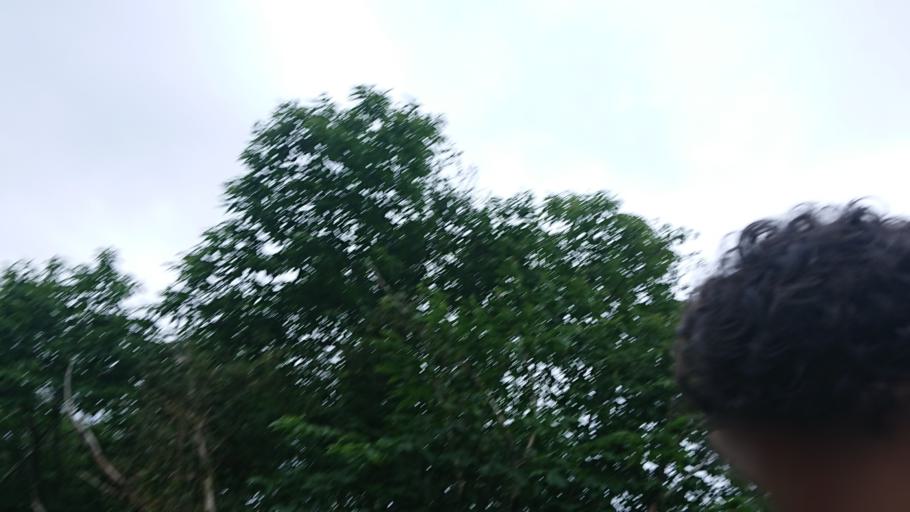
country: TR
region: Rize
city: Rize
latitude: 40.9881
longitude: 40.5062
